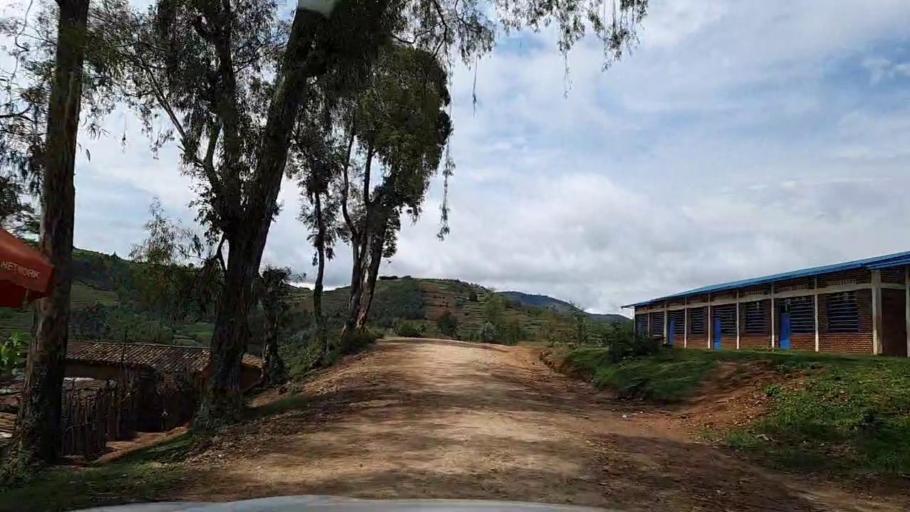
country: RW
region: Southern Province
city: Gikongoro
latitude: -2.3364
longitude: 29.5208
